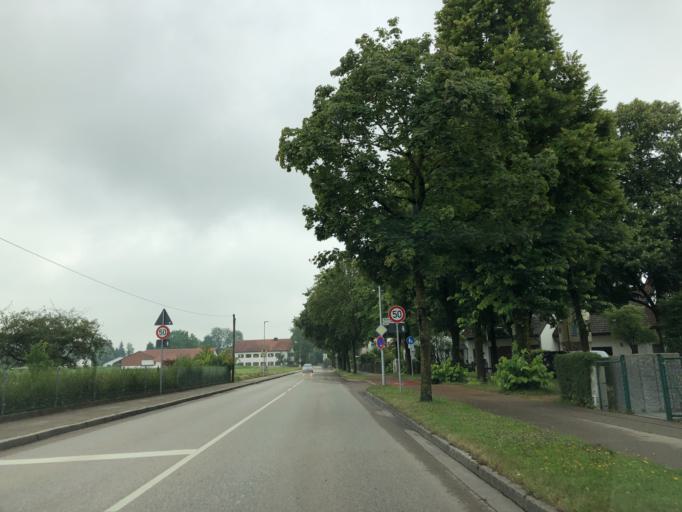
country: DE
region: Bavaria
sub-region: Upper Bavaria
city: Erding
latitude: 48.2975
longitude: 11.9094
